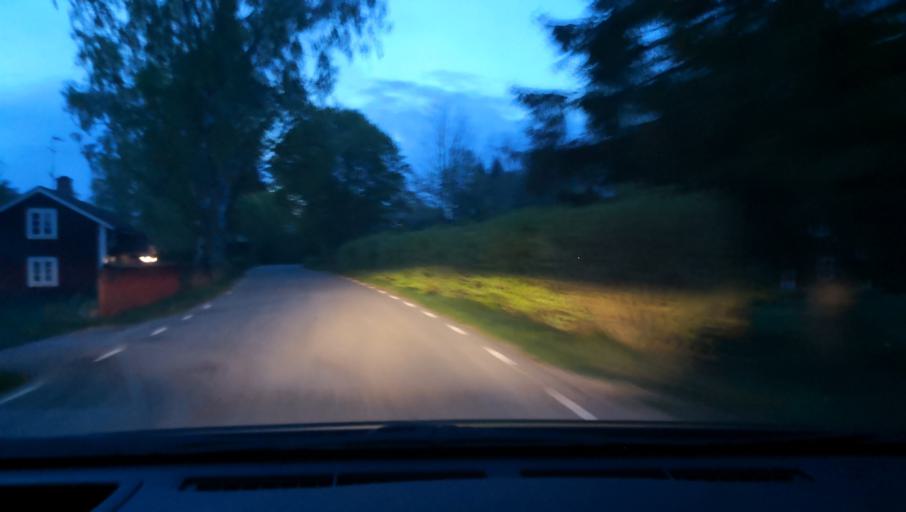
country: SE
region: OErebro
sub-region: Orebro Kommun
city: Vintrosa
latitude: 59.1743
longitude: 15.0168
